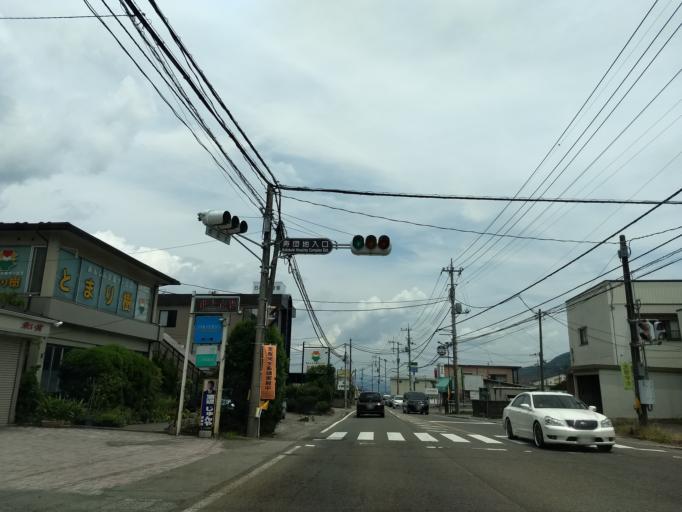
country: JP
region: Yamanashi
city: Fujikawaguchiko
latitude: 35.5086
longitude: 138.8265
